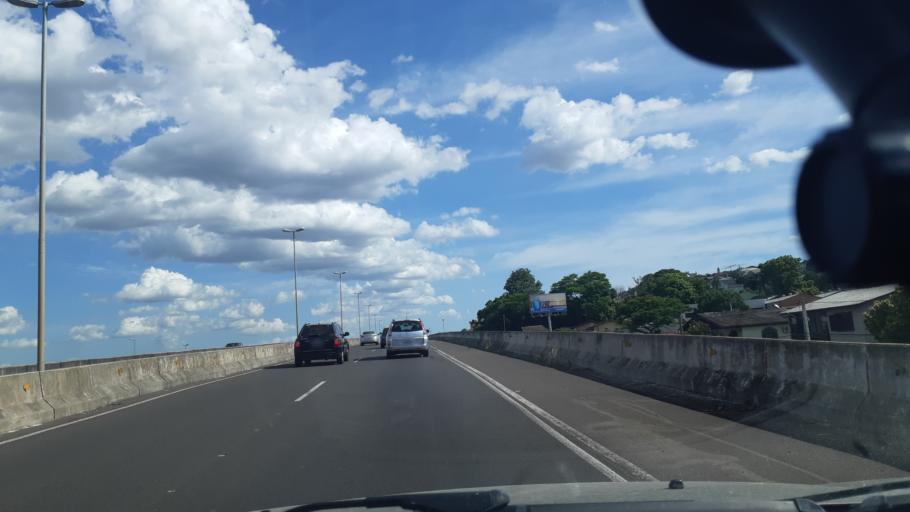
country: BR
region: Rio Grande do Sul
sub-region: Novo Hamburgo
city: Novo Hamburgo
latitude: -29.6681
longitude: -51.1433
